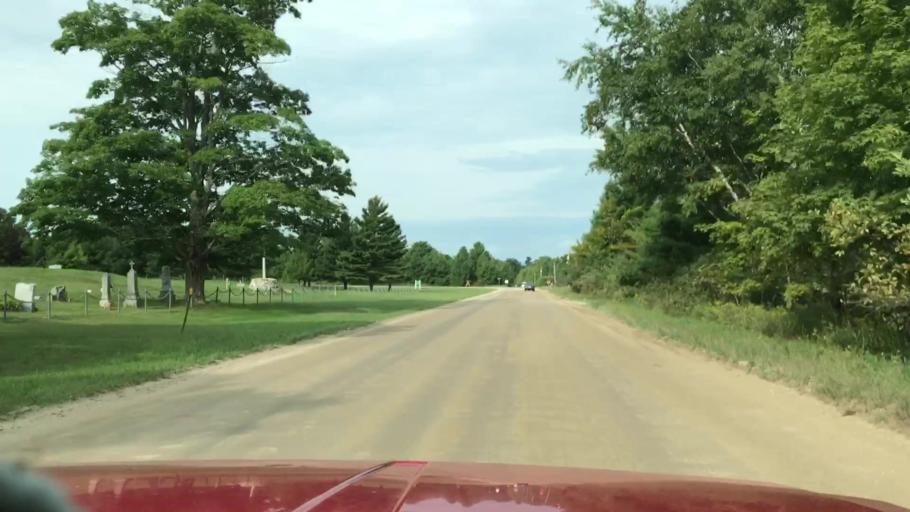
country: US
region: Michigan
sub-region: Charlevoix County
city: Charlevoix
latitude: 45.7286
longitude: -85.5233
